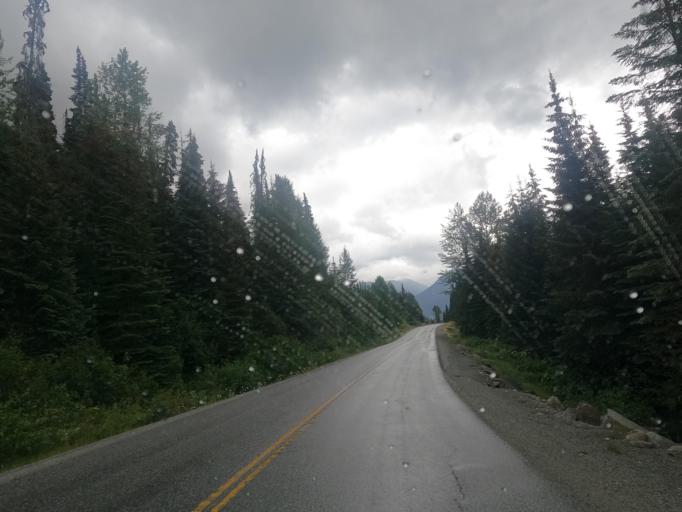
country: CA
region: British Columbia
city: Pemberton
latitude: 50.3849
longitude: -122.4386
